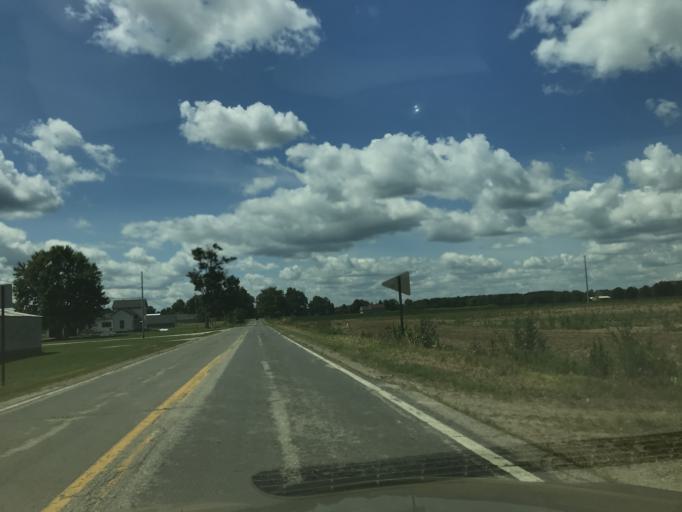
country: US
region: Michigan
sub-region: Ingham County
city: Leslie
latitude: 42.4512
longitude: -84.4692
